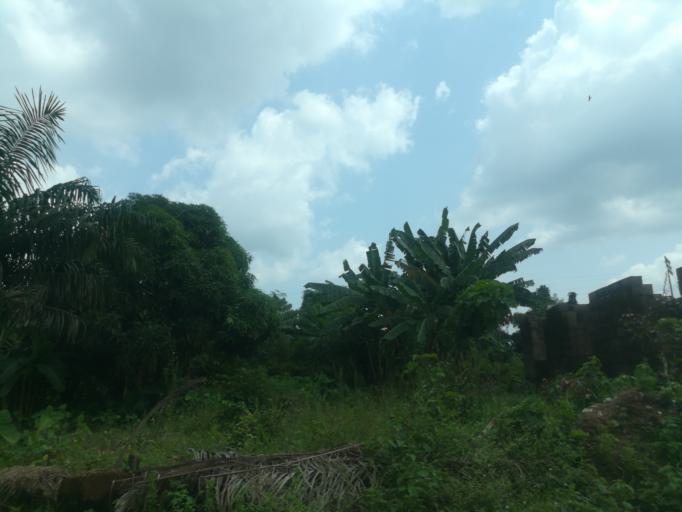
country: NG
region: Oyo
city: Ibadan
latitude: 7.4380
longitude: 3.9374
